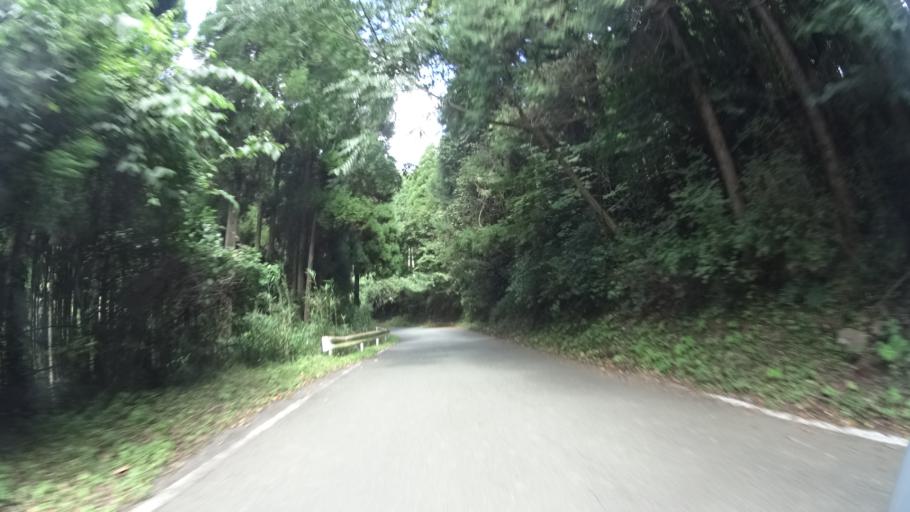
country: JP
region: Kumamoto
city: Aso
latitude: 32.8131
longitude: 131.1326
